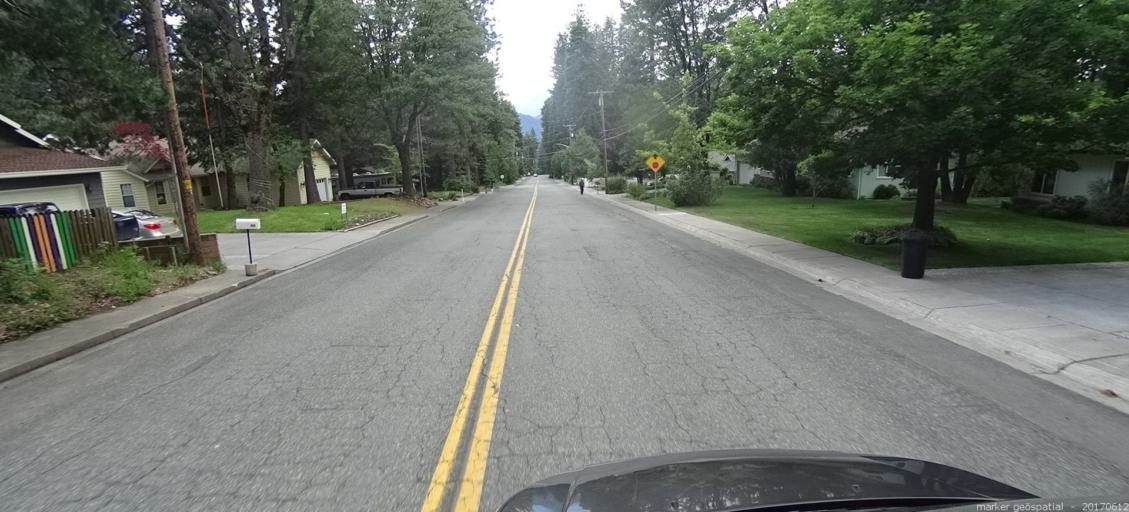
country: US
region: California
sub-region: Siskiyou County
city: Mount Shasta
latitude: 41.3122
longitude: -122.3006
